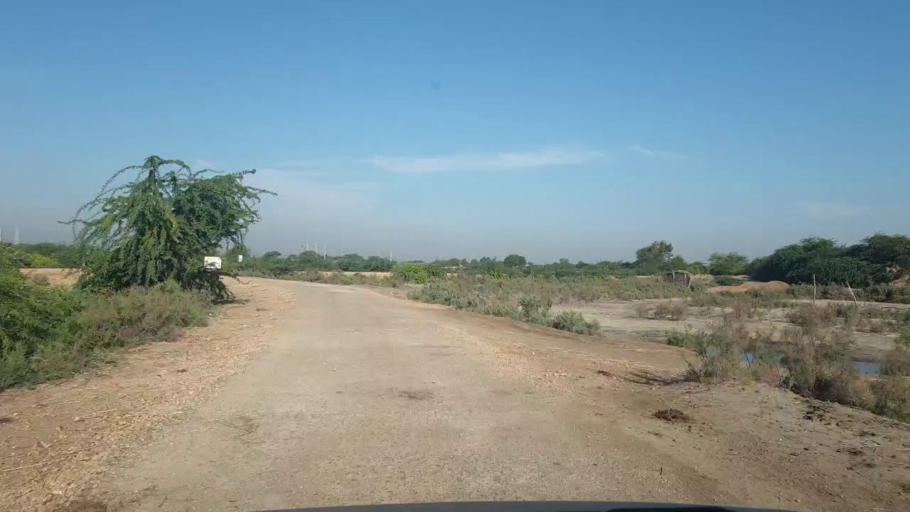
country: PK
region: Sindh
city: Talhar
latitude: 24.8299
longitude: 68.8183
